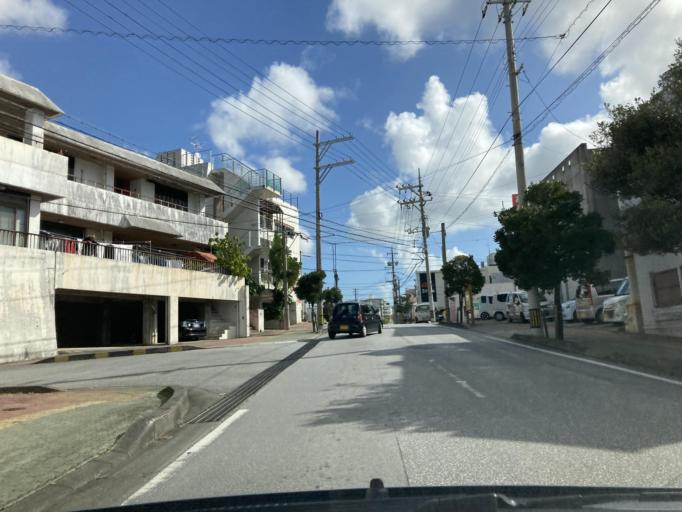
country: JP
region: Okinawa
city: Naha-shi
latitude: 26.2341
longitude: 127.7181
